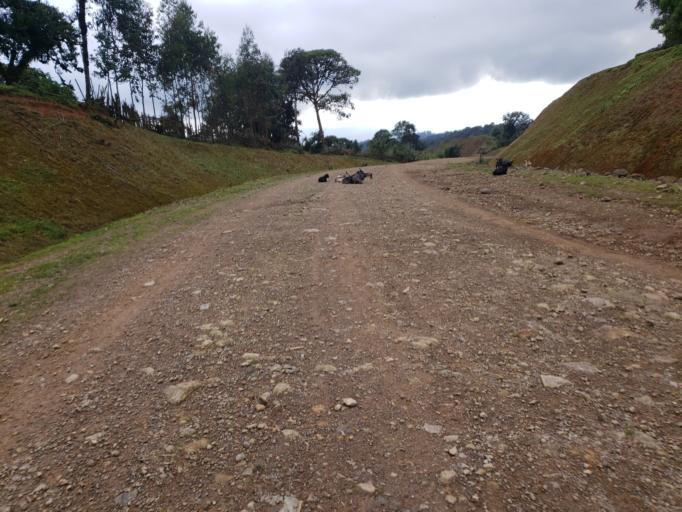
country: ET
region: Oromiya
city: Dodola
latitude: 6.6842
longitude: 39.3680
